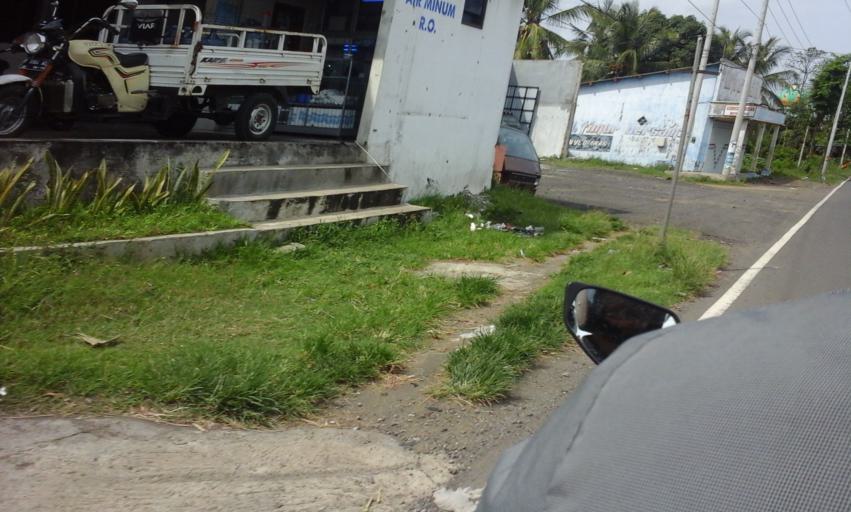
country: ID
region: East Java
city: Kepuh Wetan
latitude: -8.2583
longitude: 114.3372
